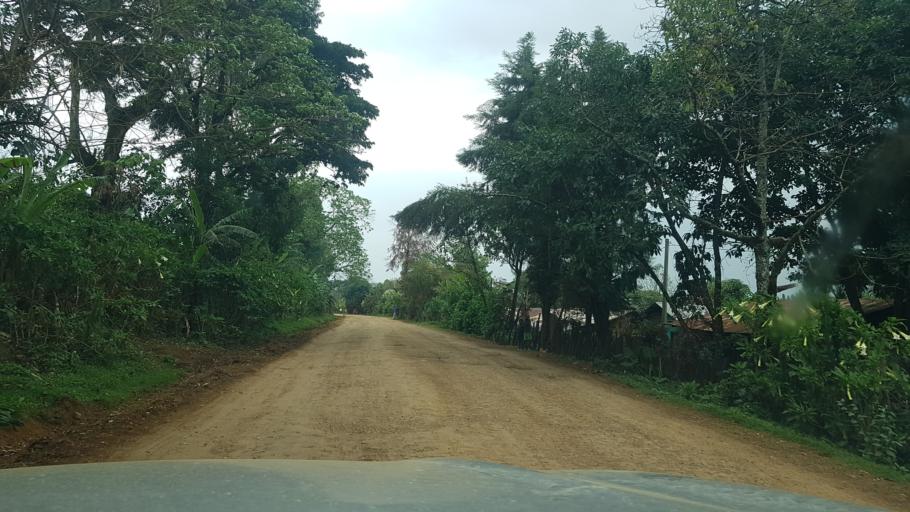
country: ET
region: Oromiya
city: Gore
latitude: 7.8317
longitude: 35.4674
